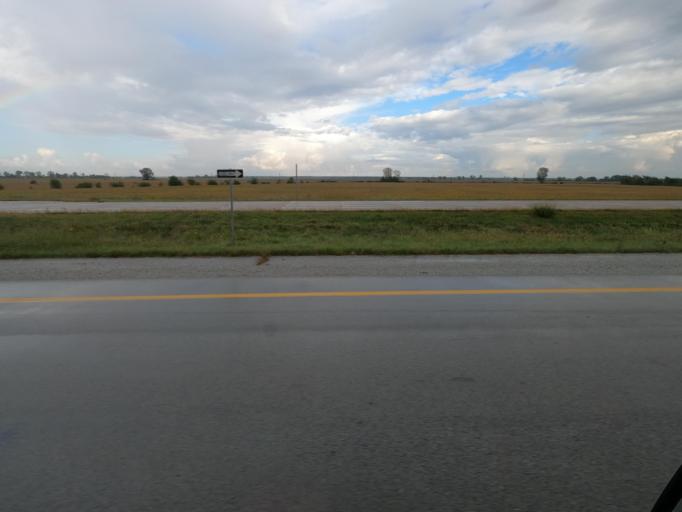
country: US
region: Illinois
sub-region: Hancock County
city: Warsaw
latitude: 40.2884
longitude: -91.5681
